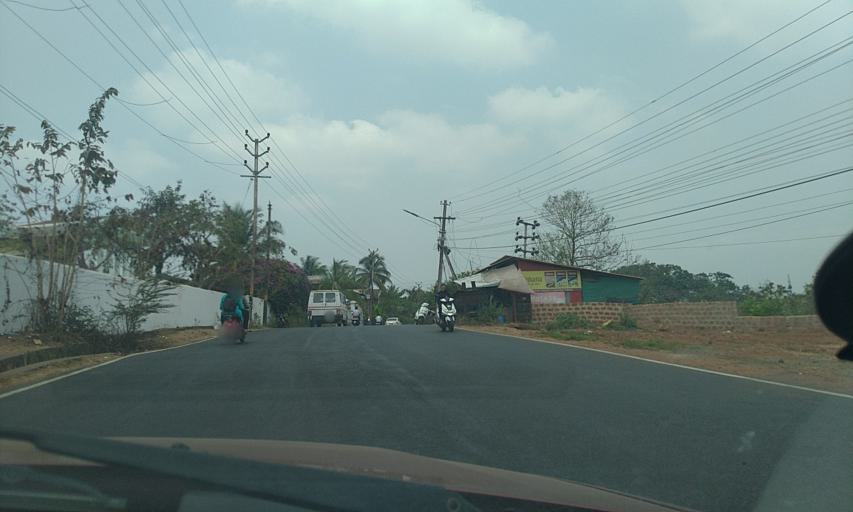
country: IN
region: Goa
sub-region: North Goa
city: Mapuca
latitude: 15.6009
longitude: 73.8080
